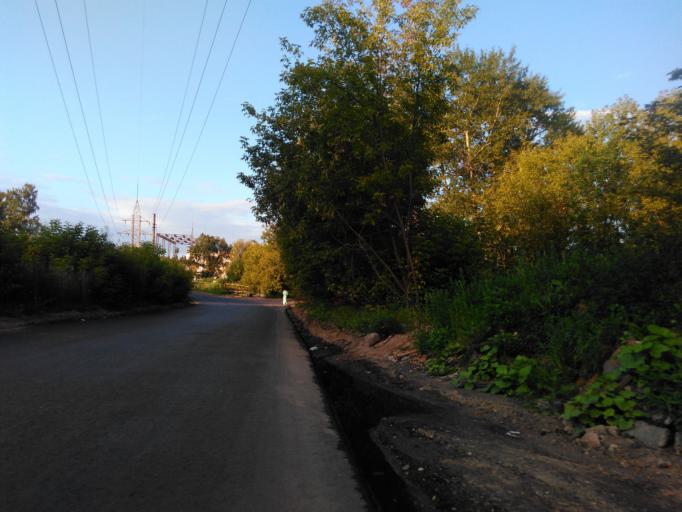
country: RU
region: Moskovskaya
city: Bogorodskoye
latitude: 55.8185
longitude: 37.6933
